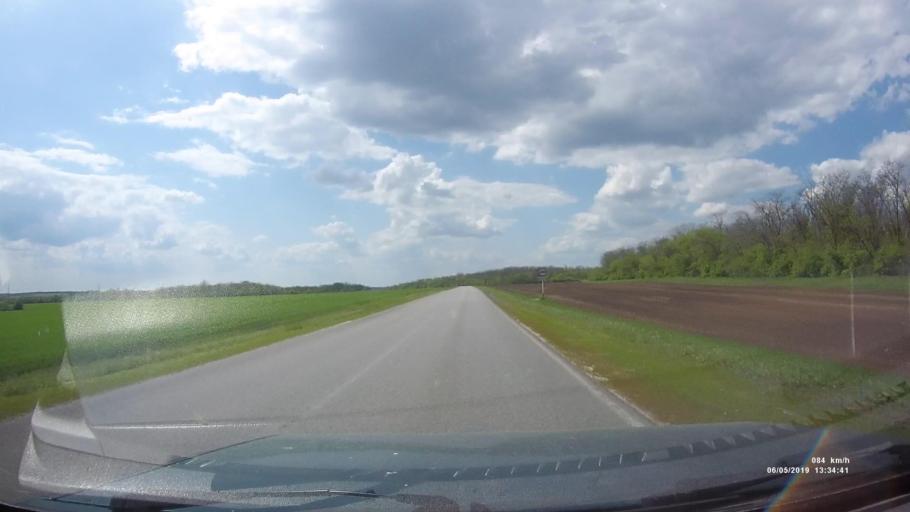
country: RU
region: Rostov
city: Ust'-Donetskiy
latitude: 47.6933
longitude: 40.7583
